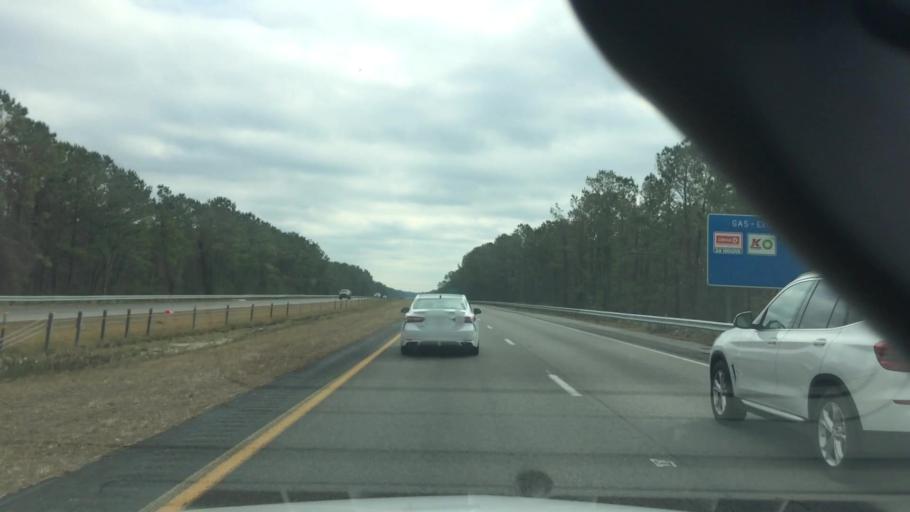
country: US
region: North Carolina
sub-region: New Hanover County
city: Castle Hayne
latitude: 34.3580
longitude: -77.8876
